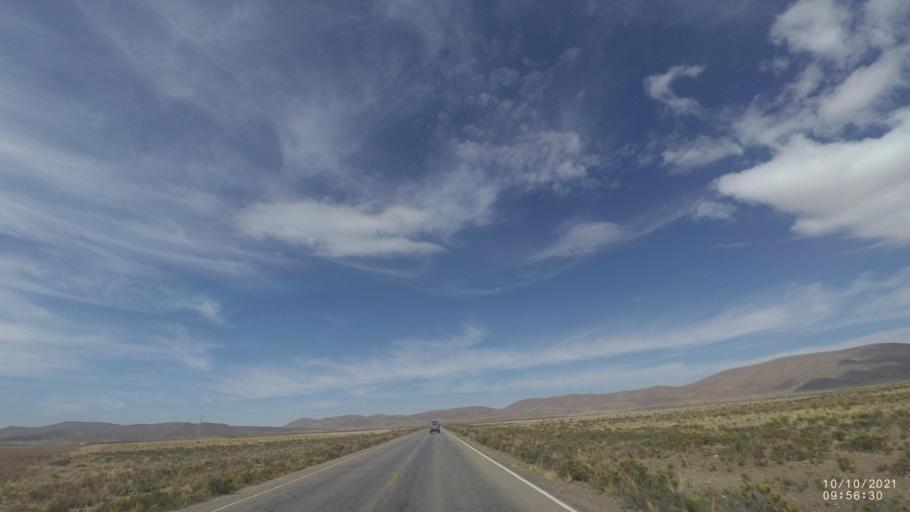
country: BO
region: La Paz
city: Colquiri
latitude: -17.3231
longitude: -67.3756
